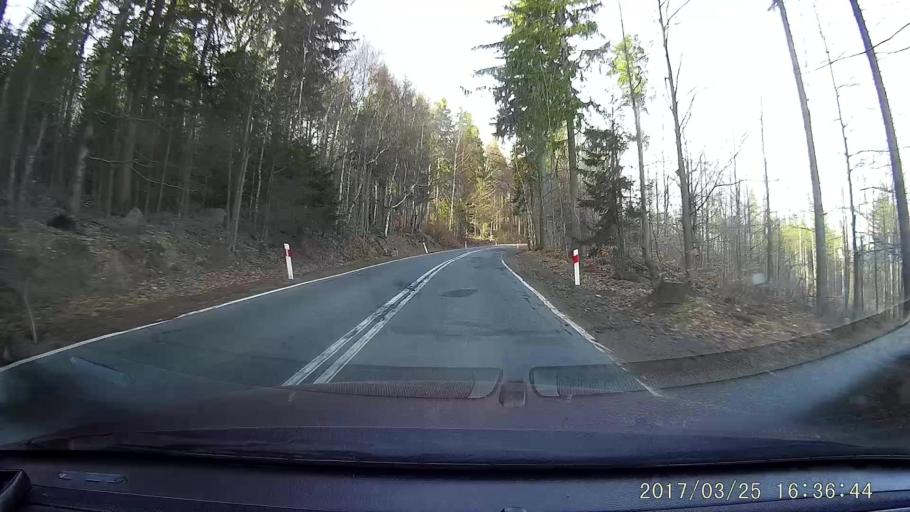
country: PL
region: Lower Silesian Voivodeship
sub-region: Powiat jeleniogorski
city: Szklarska Poreba
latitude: 50.8450
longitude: 15.5248
